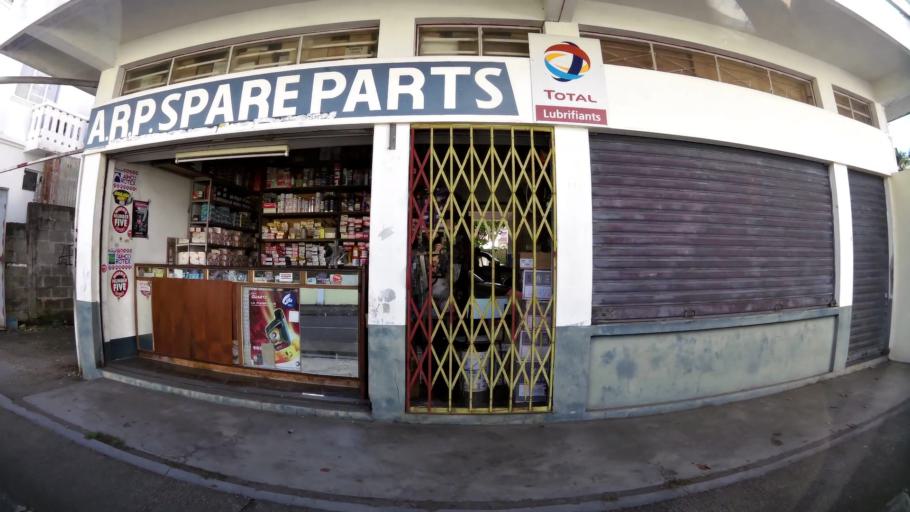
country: MU
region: Grand Port
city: Mahebourg
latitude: -20.4120
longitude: 57.7104
